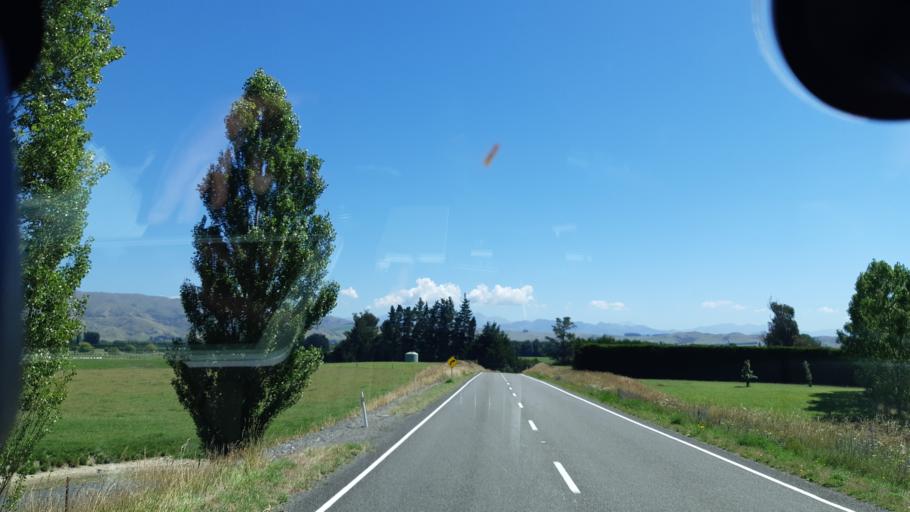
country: NZ
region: Canterbury
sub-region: Kaikoura District
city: Kaikoura
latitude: -42.7479
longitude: 173.2677
